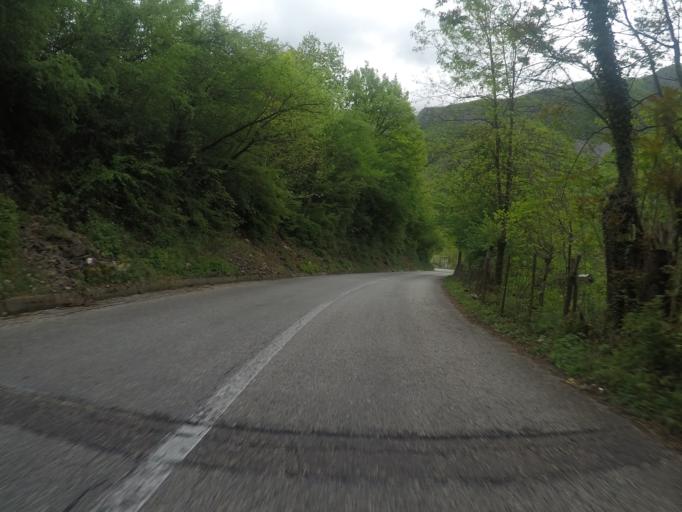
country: BA
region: Federation of Bosnia and Herzegovina
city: Siroki Brijeg
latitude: 43.5384
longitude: 17.6063
